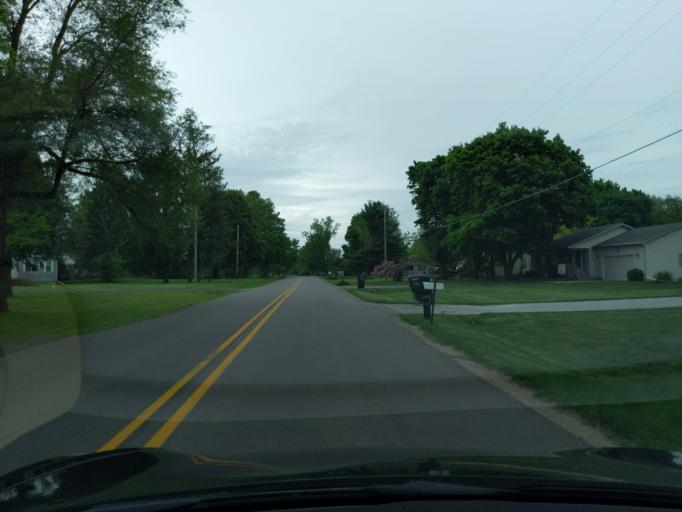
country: US
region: Michigan
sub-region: Ingham County
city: Leslie
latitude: 42.3809
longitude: -84.3492
